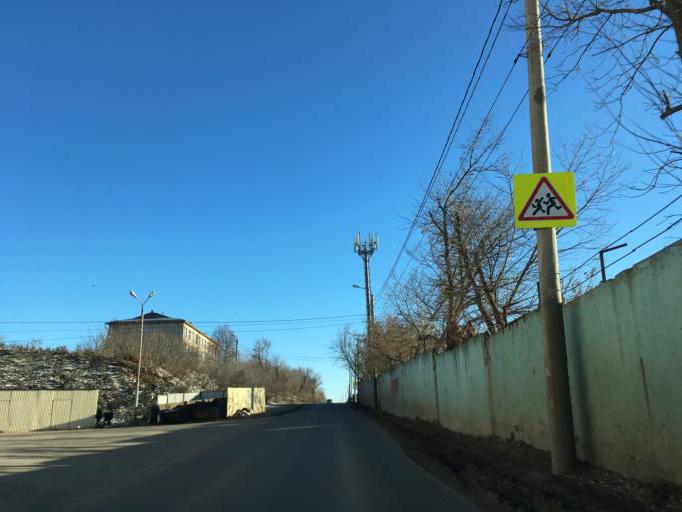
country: RU
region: Tula
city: Tula
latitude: 54.1943
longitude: 37.6658
